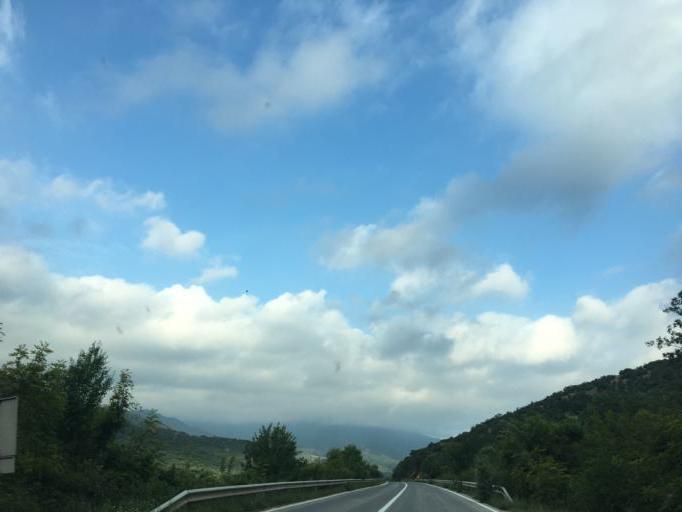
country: MK
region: Demir Kapija
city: Demir Kapija
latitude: 41.3917
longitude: 22.3492
